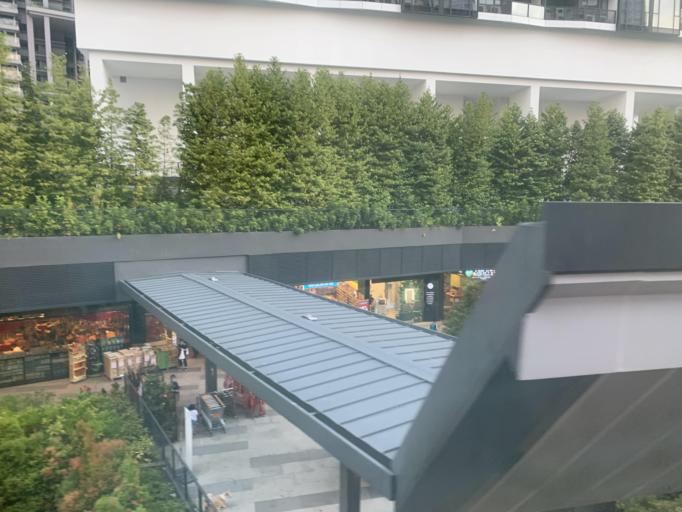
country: SG
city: Singapore
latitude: 1.2899
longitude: 103.8167
